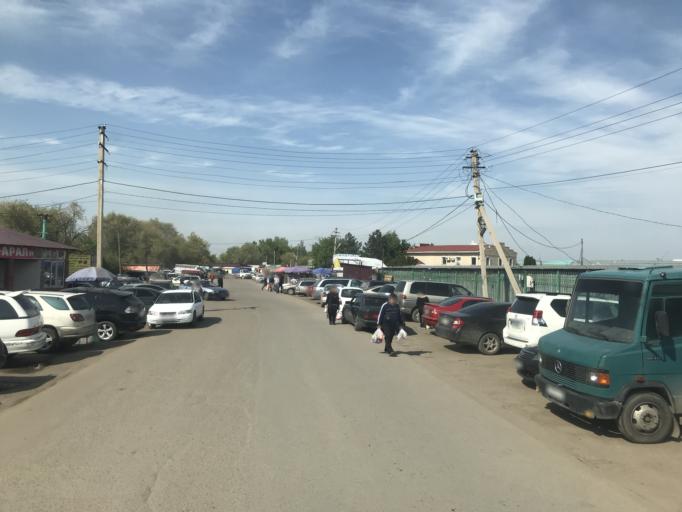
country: KZ
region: Almaty Oblysy
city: Burunday
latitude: 43.2319
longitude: 76.7701
